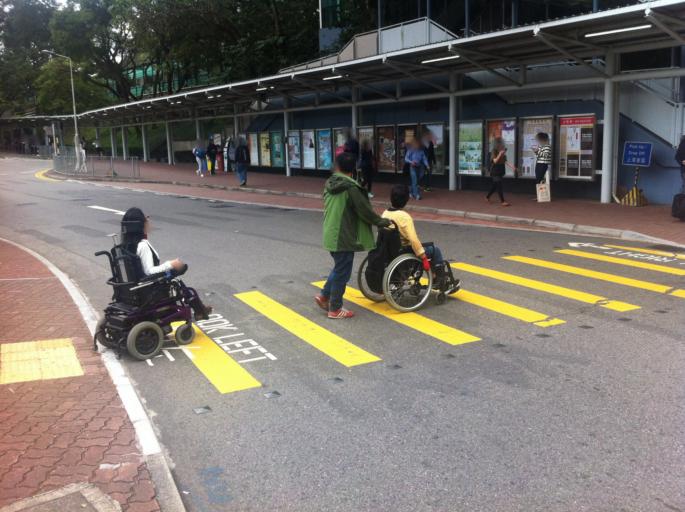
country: HK
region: Sha Tin
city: Sha Tin
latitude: 22.4141
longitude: 114.2098
